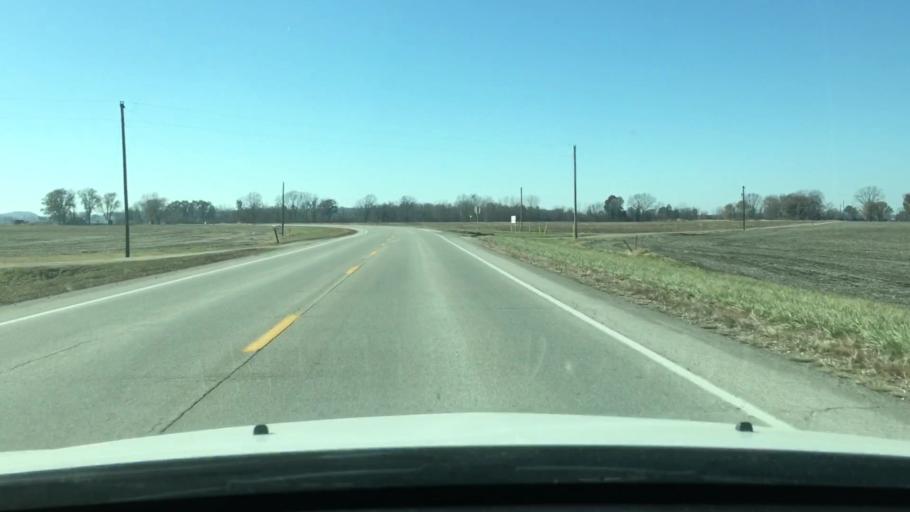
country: US
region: Missouri
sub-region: Pike County
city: Louisiana
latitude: 39.4997
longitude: -90.9982
